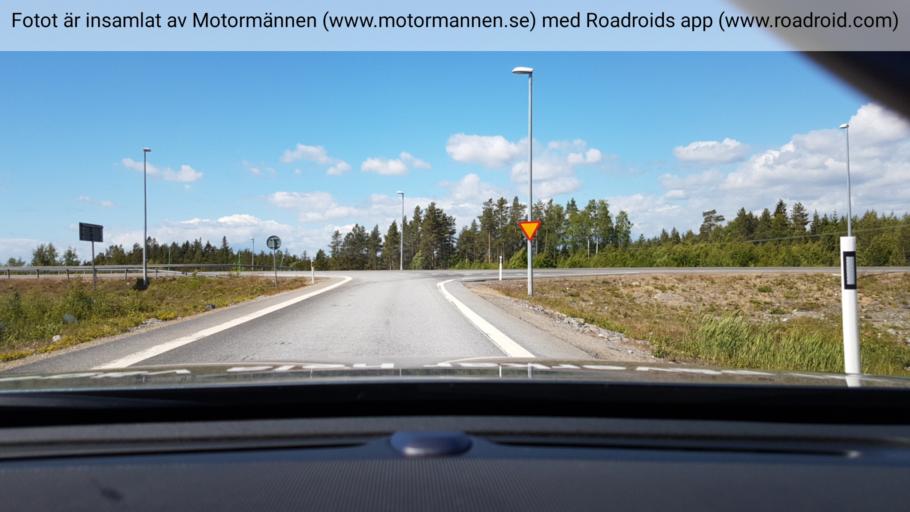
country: SE
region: Vaesterbotten
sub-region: Nordmalings Kommun
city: Nordmaling
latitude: 63.5835
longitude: 19.5374
